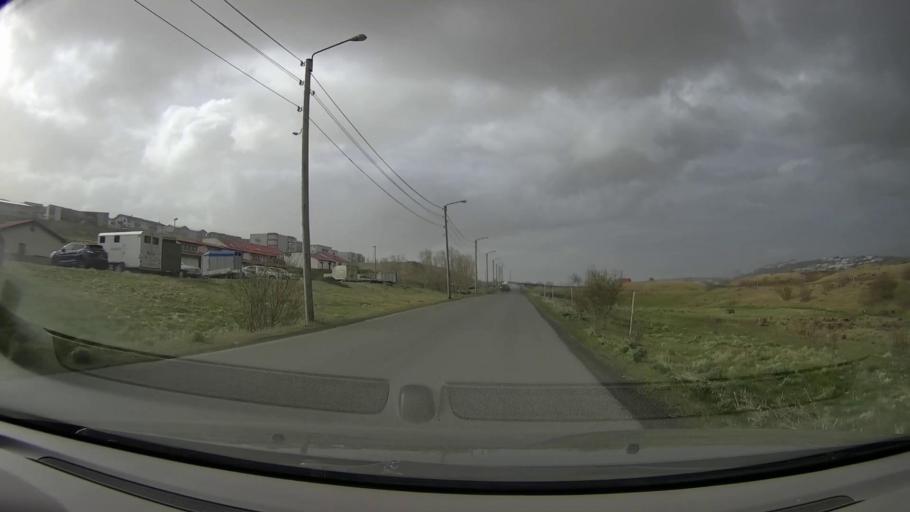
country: IS
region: Capital Region
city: Hafnarfjoerdur
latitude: 64.0531
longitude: -21.9270
